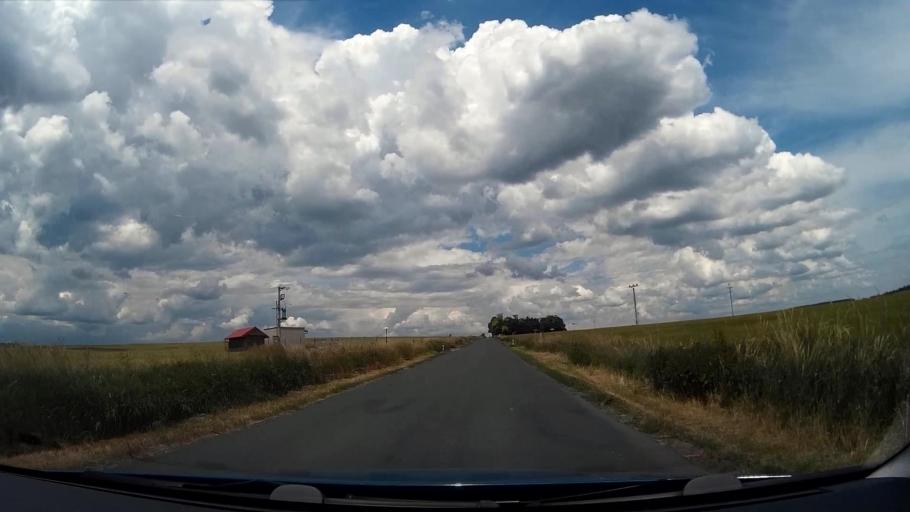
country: CZ
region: South Moravian
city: Orechov
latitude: 49.0956
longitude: 16.5263
